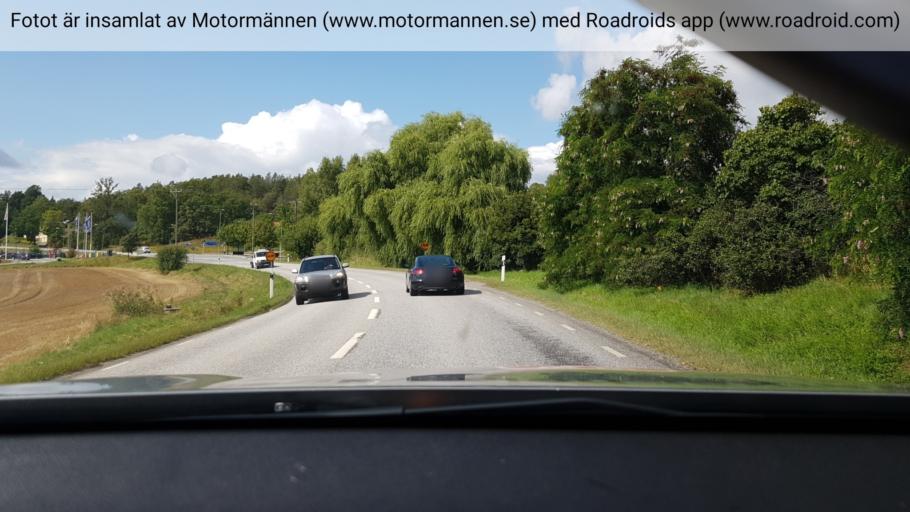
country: SE
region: Stockholm
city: Stenhamra
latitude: 59.2869
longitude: 17.7189
